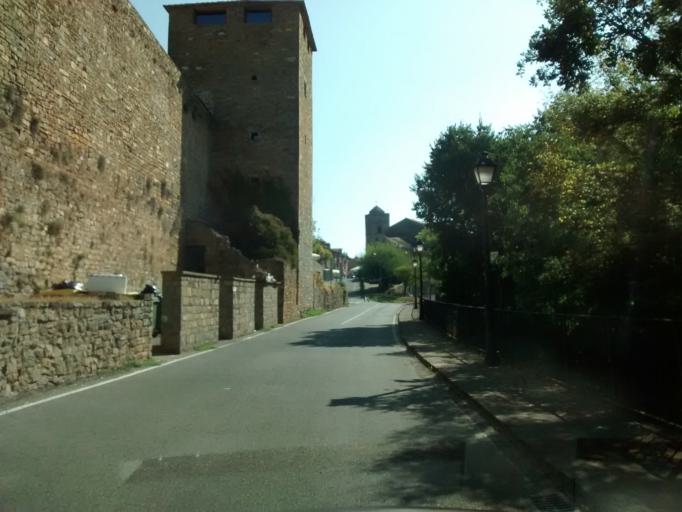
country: ES
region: Aragon
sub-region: Provincia de Huesca
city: Ainsa
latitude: 42.4178
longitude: 0.1364
